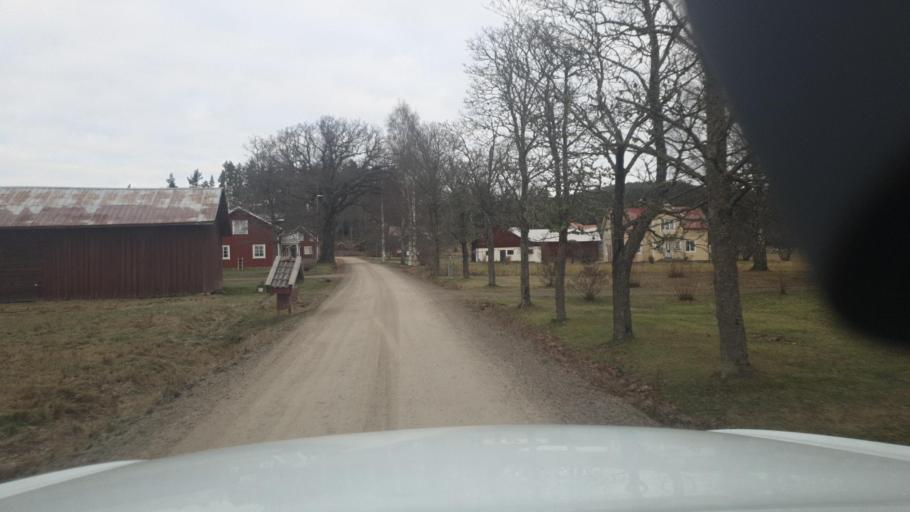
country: SE
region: Vaermland
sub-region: Sunne Kommun
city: Sunne
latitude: 59.8143
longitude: 13.0565
